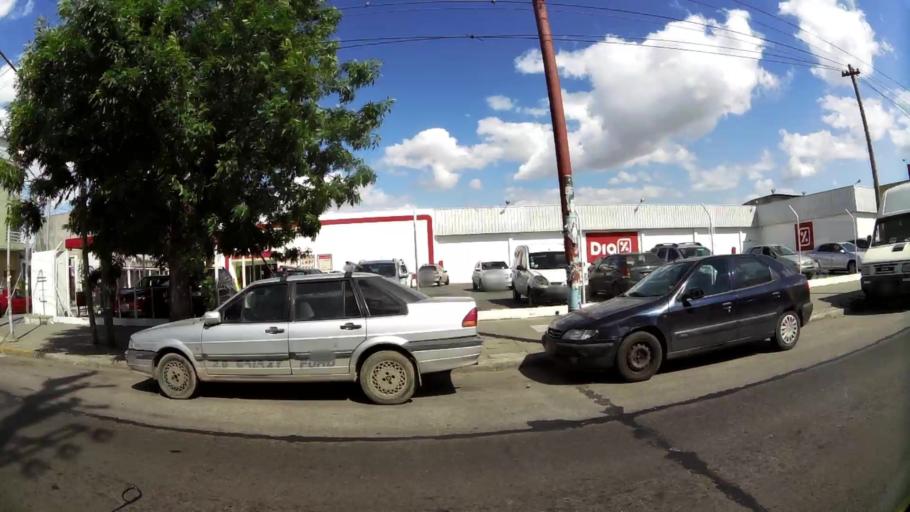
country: AR
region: Buenos Aires
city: San Justo
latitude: -34.6576
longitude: -58.5409
